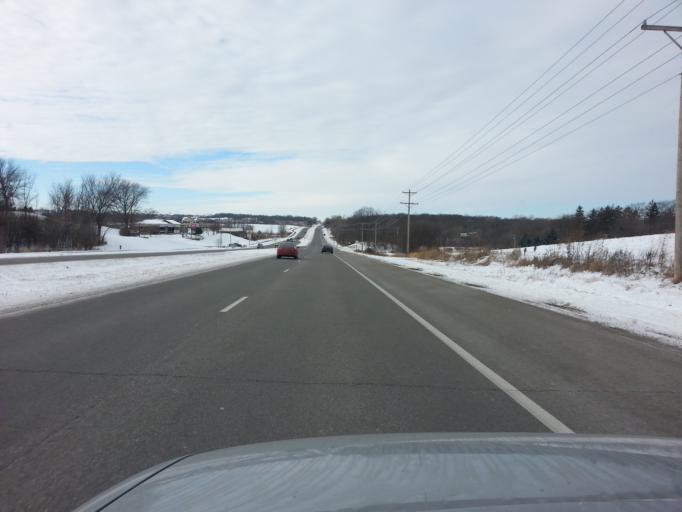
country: US
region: Minnesota
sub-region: Scott County
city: Prior Lake
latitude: 44.7470
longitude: -93.4261
